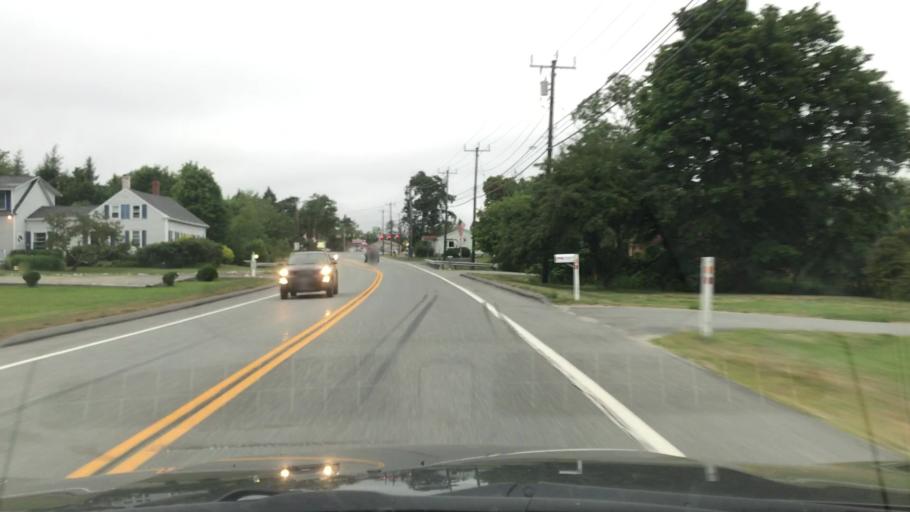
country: US
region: Maine
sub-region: Hancock County
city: Trenton
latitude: 44.4365
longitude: -68.3691
